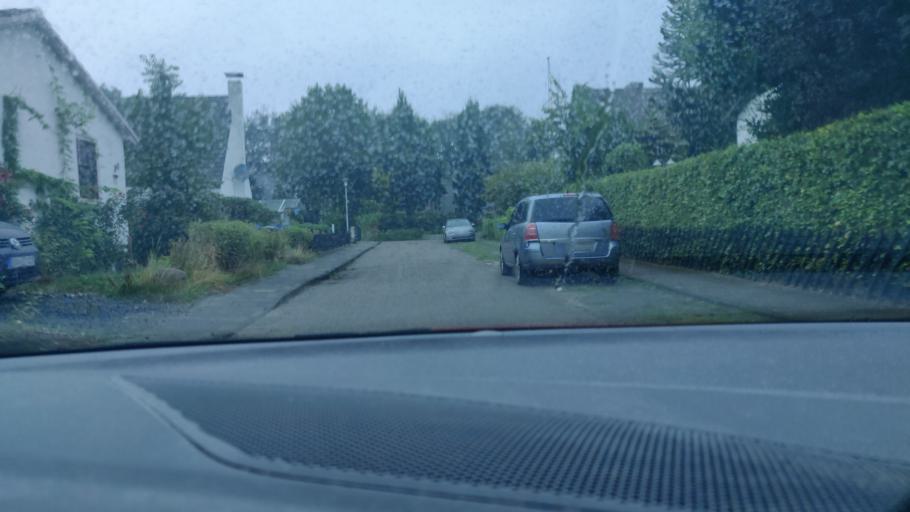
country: DE
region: Lower Saxony
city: Nordholz
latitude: 53.8637
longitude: 8.6100
